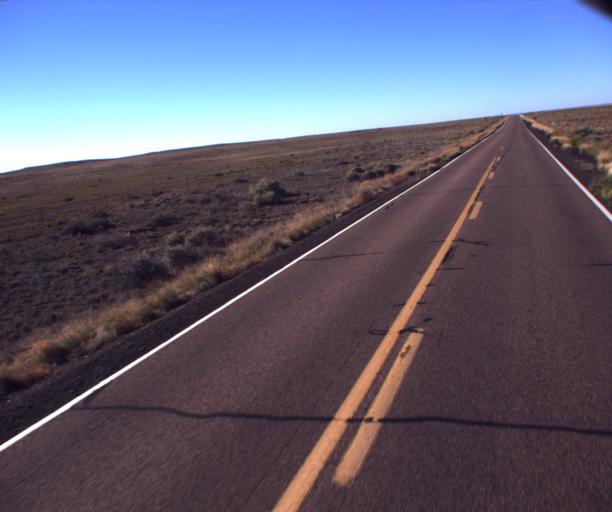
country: US
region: Arizona
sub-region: Navajo County
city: Holbrook
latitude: 34.8354
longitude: -110.1848
